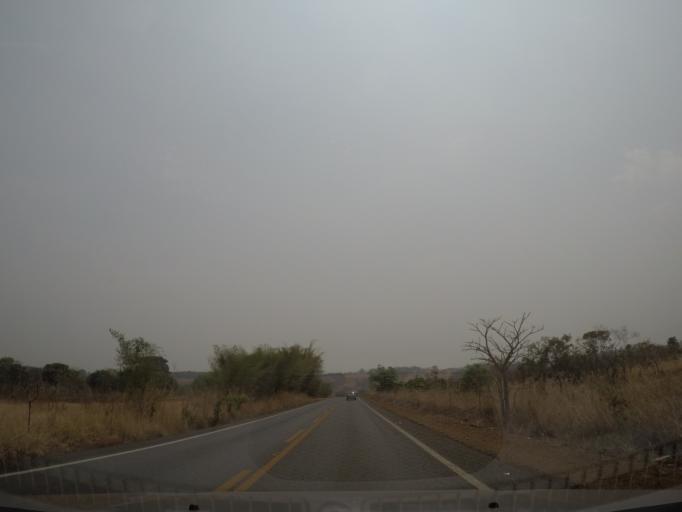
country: BR
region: Goias
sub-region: Pirenopolis
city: Pirenopolis
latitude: -15.8907
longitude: -48.8924
